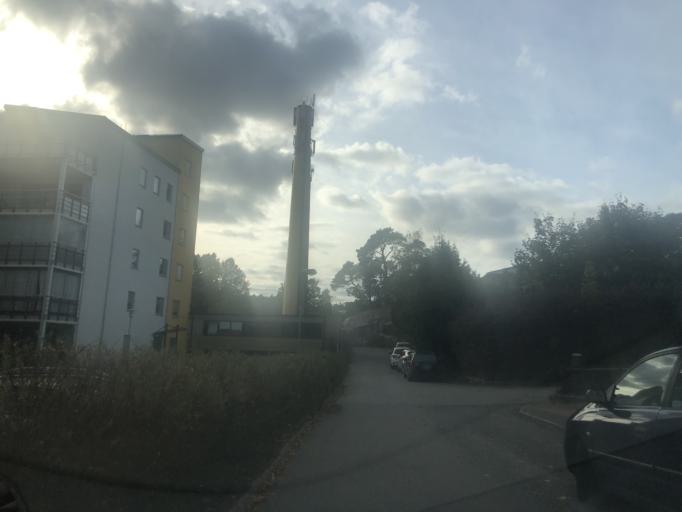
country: SE
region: Vaestra Goetaland
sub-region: Goteborg
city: Majorna
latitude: 57.6339
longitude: 11.9364
